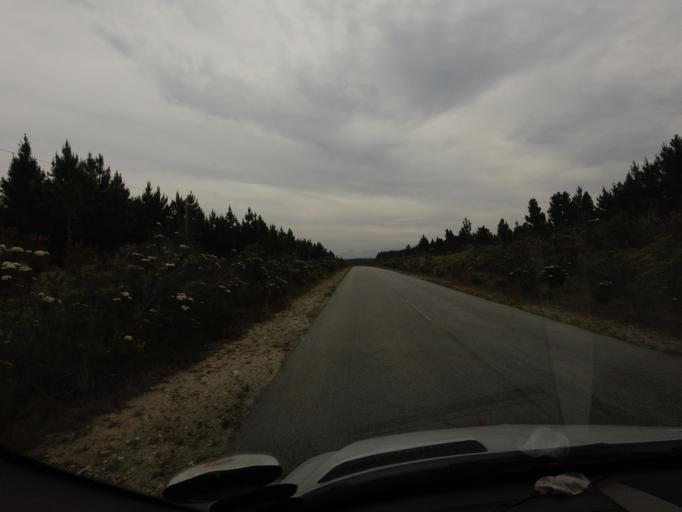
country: ZA
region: Eastern Cape
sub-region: Cacadu District Municipality
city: Kareedouw
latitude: -34.0016
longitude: 23.8586
